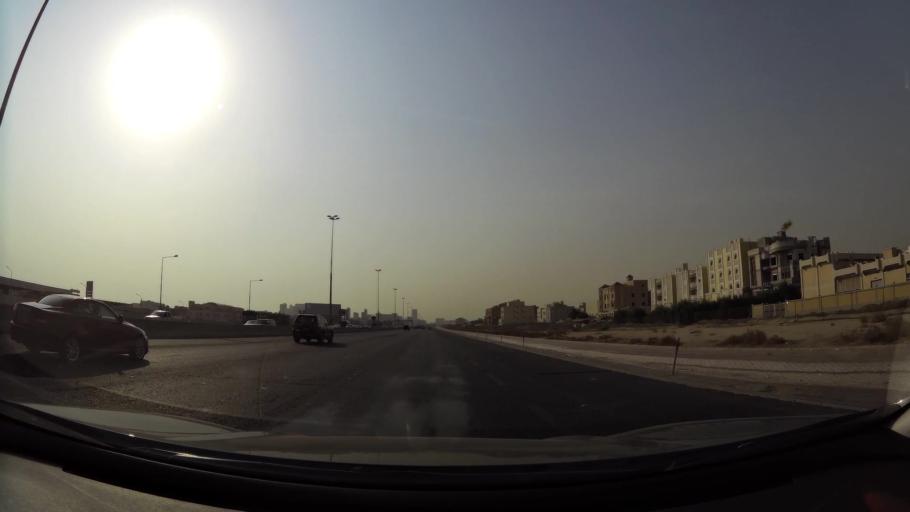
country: KW
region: Mubarak al Kabir
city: Mubarak al Kabir
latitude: 29.1952
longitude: 48.1085
